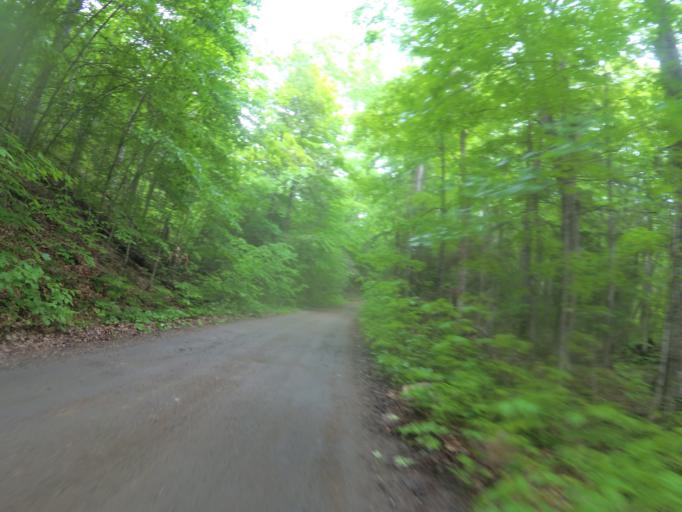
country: CA
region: Ontario
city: Renfrew
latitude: 45.1150
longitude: -76.8222
